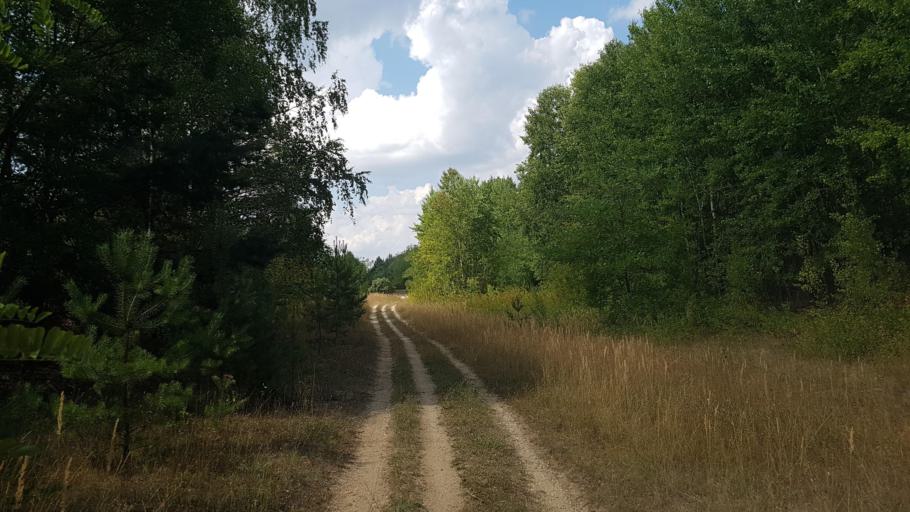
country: DE
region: Brandenburg
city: Sallgast
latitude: 51.5637
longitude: 13.8469
